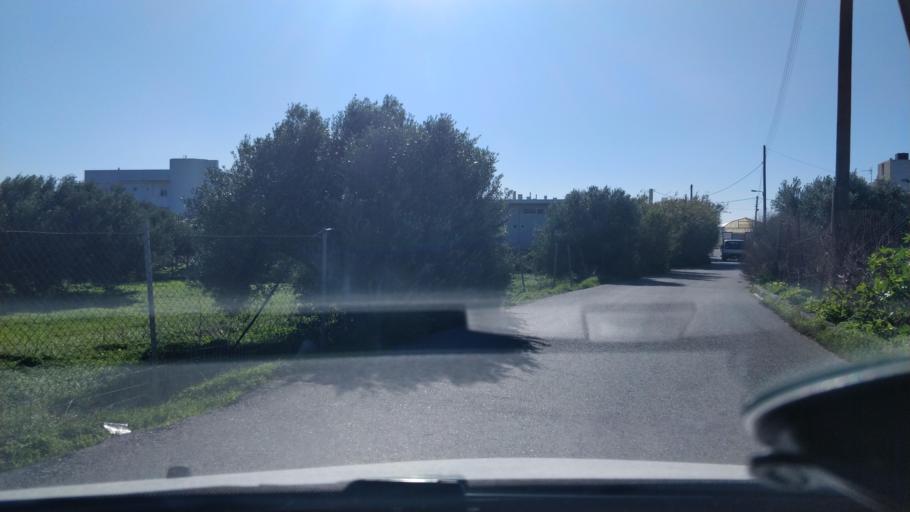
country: GR
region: Crete
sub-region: Nomos Lasithiou
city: Gra Liyia
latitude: 35.0145
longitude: 25.6770
